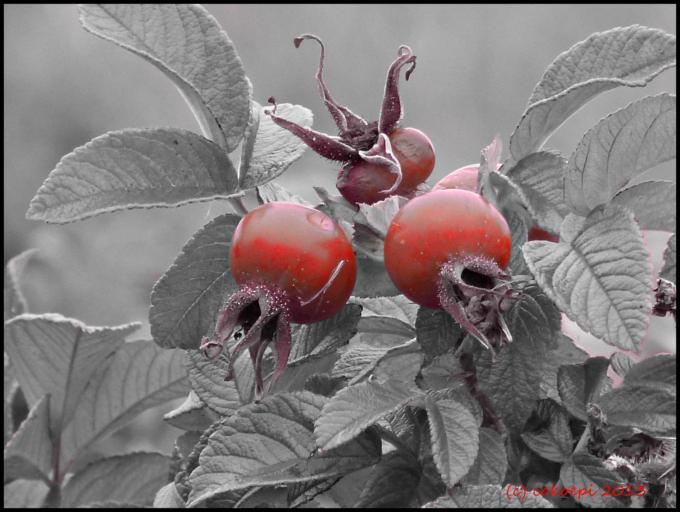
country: DE
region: Schleswig-Holstein
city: Sankt Peter-Ording
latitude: 54.2977
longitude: 8.6350
